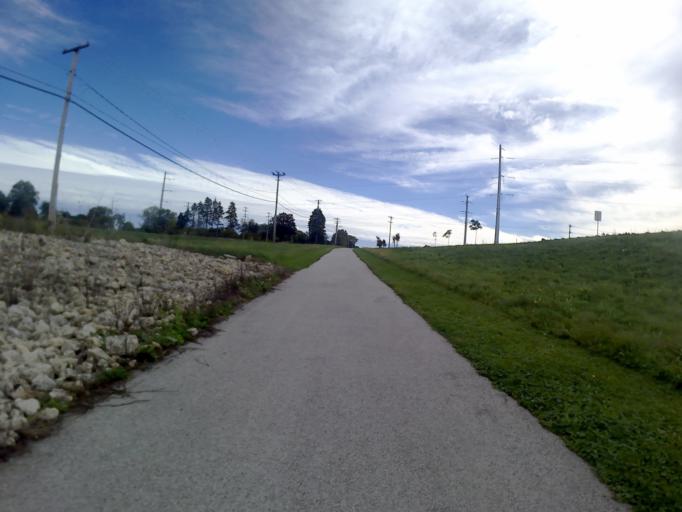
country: US
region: Illinois
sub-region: Kane County
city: South Elgin
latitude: 41.9773
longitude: -88.2682
